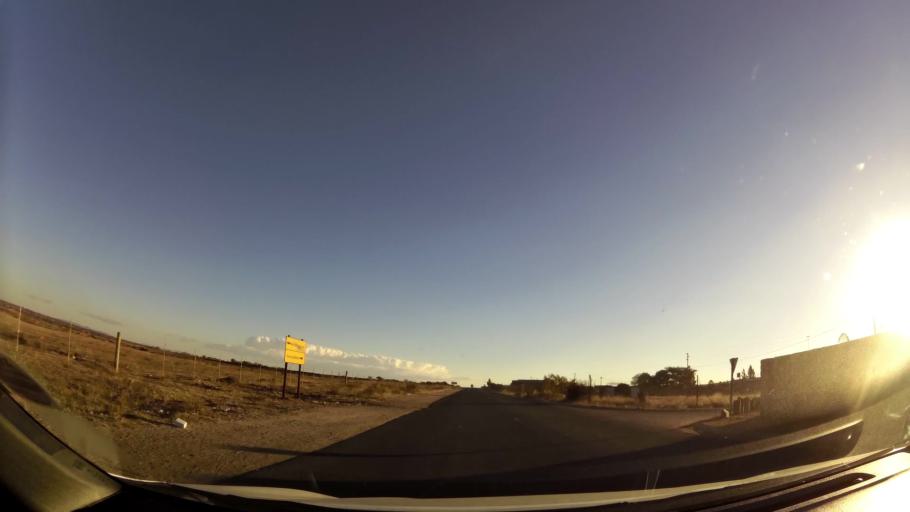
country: ZA
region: Limpopo
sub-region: Capricorn District Municipality
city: Polokwane
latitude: -23.8320
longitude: 29.3706
